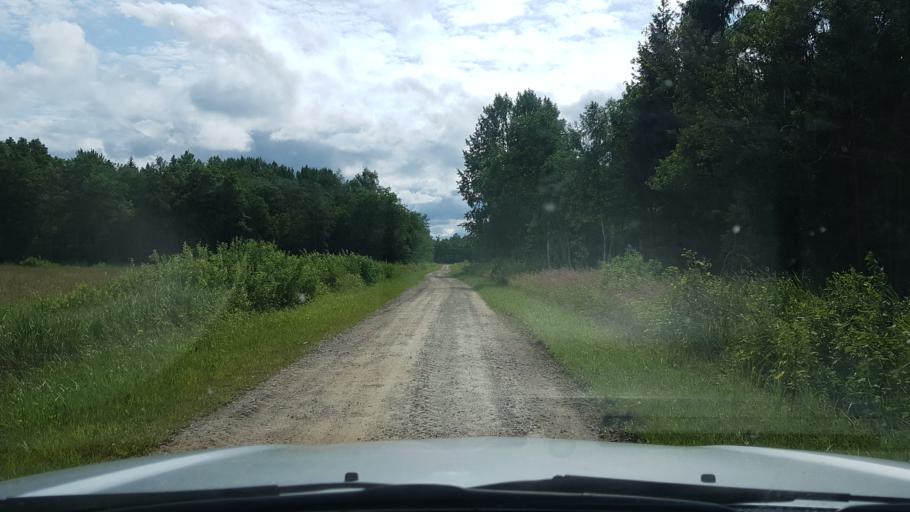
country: EE
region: Ida-Virumaa
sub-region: Narva-Joesuu linn
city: Narva-Joesuu
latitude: 59.3661
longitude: 27.9244
